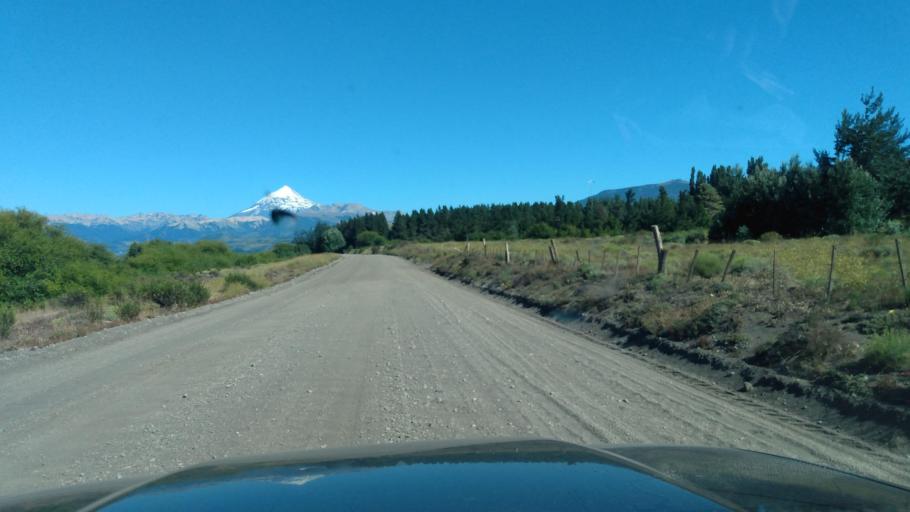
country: AR
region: Neuquen
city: Junin de los Andes
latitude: -39.7877
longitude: -71.2214
